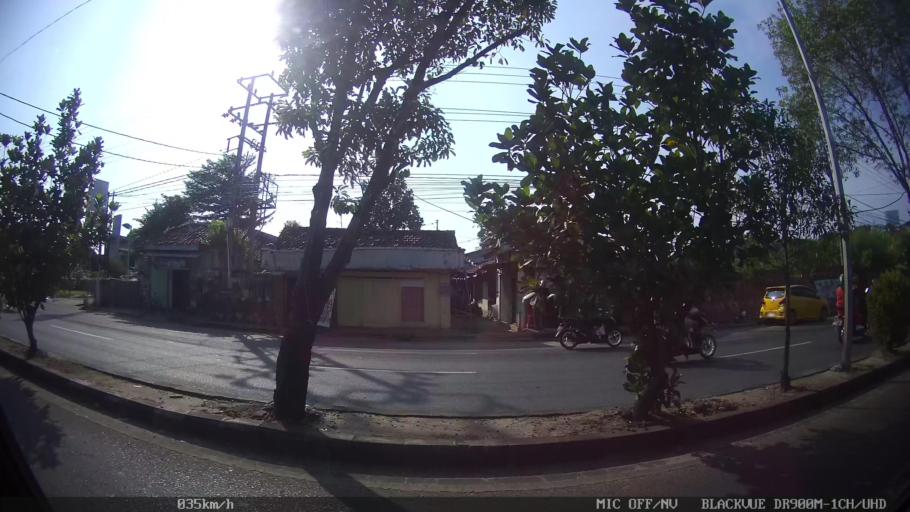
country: ID
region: Lampung
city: Bandarlampung
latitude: -5.4053
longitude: 105.2591
